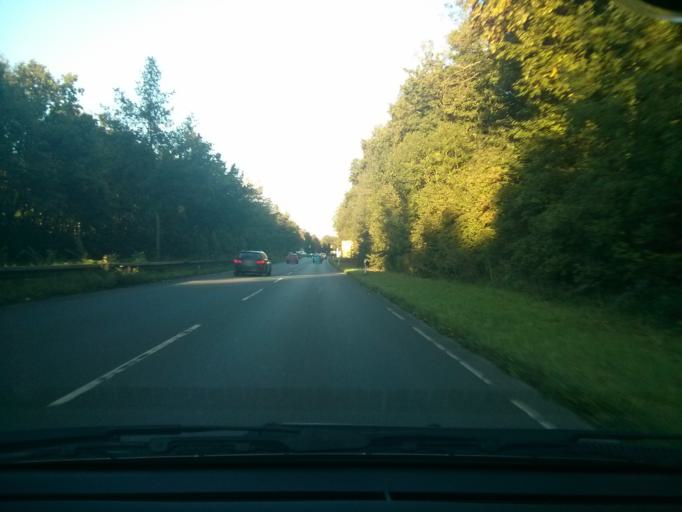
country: DE
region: North Rhine-Westphalia
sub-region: Regierungsbezirk Arnsberg
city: Holzwickede
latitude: 51.5218
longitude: 7.6430
